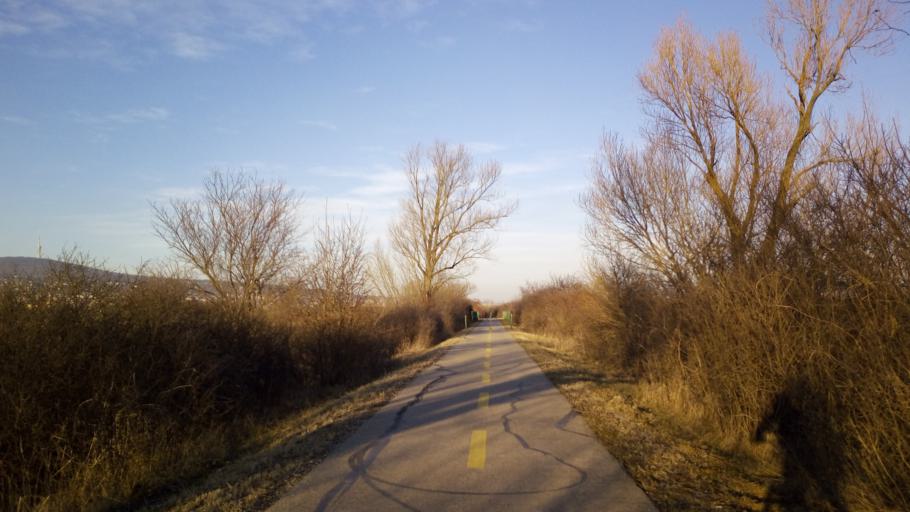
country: HU
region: Baranya
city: Pellerd
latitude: 46.0502
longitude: 18.1957
